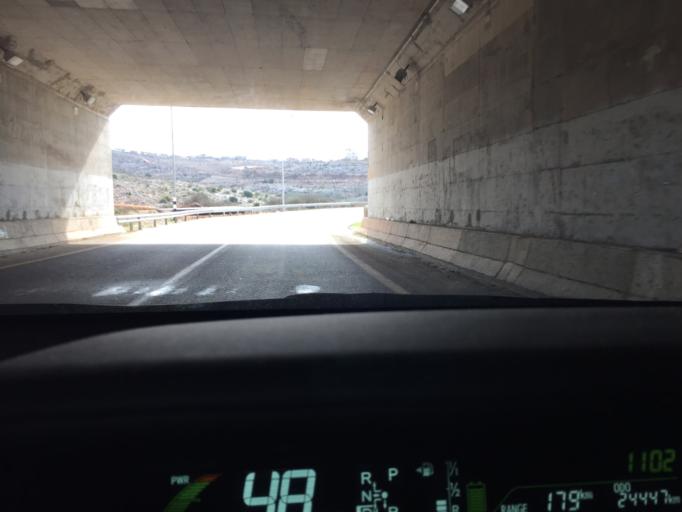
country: PS
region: West Bank
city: Sartah
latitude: 32.0935
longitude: 35.1069
